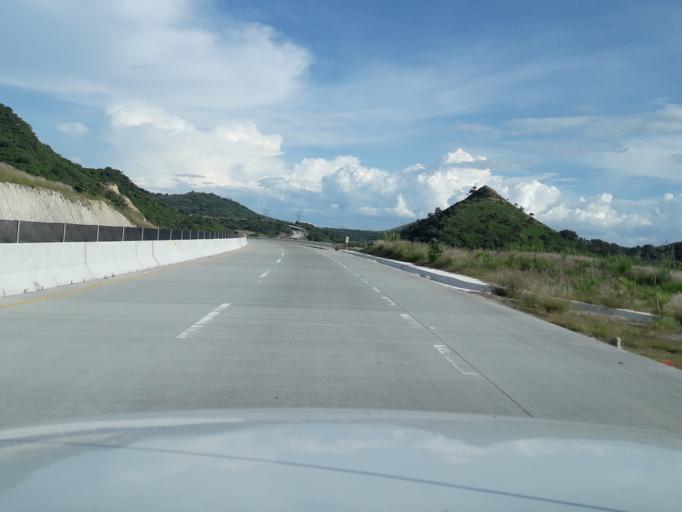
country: MX
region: Jalisco
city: Tala
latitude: 20.6009
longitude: -103.6767
